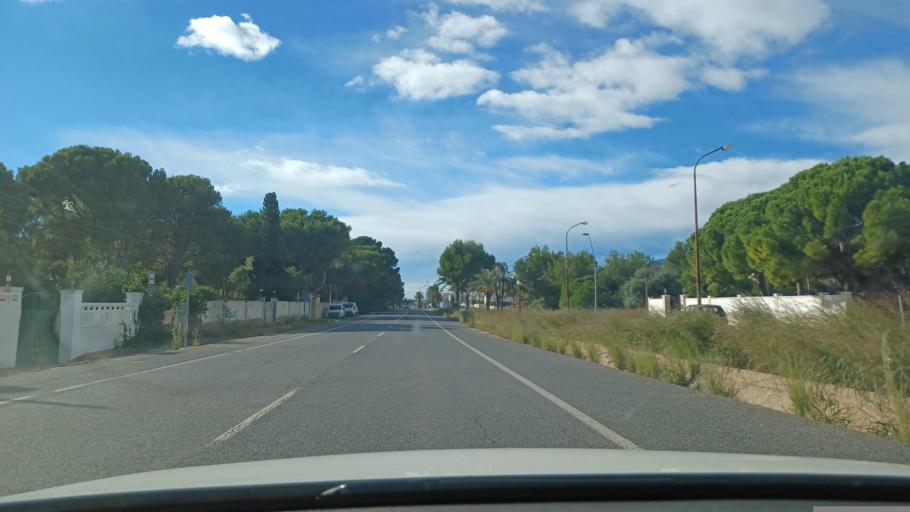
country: ES
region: Catalonia
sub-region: Provincia de Tarragona
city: Sant Carles de la Rapita
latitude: 40.5980
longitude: 0.5729
